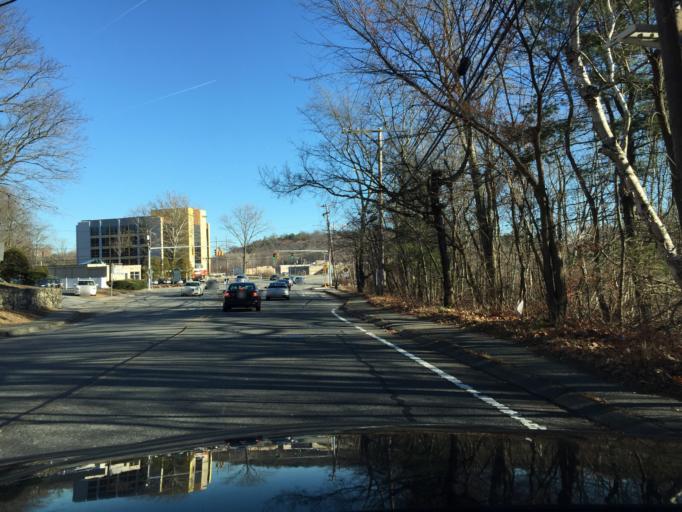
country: US
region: Massachusetts
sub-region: Middlesex County
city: Woburn
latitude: 42.4613
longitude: -71.1691
